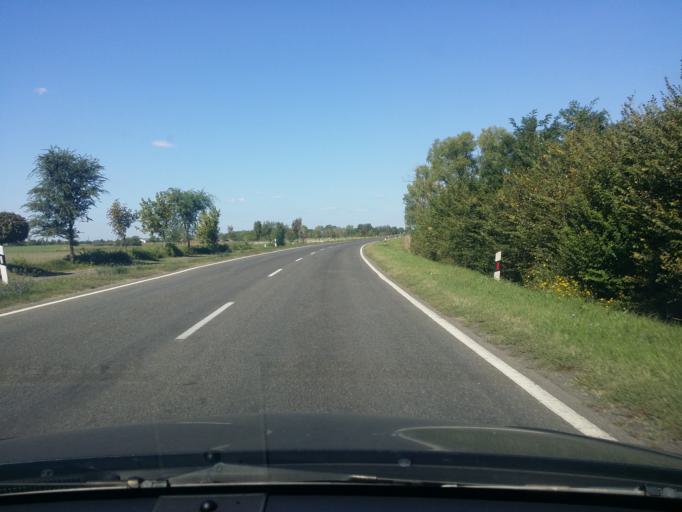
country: HU
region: Bacs-Kiskun
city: Kiskunfelegyhaza
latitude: 46.6740
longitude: 19.8550
